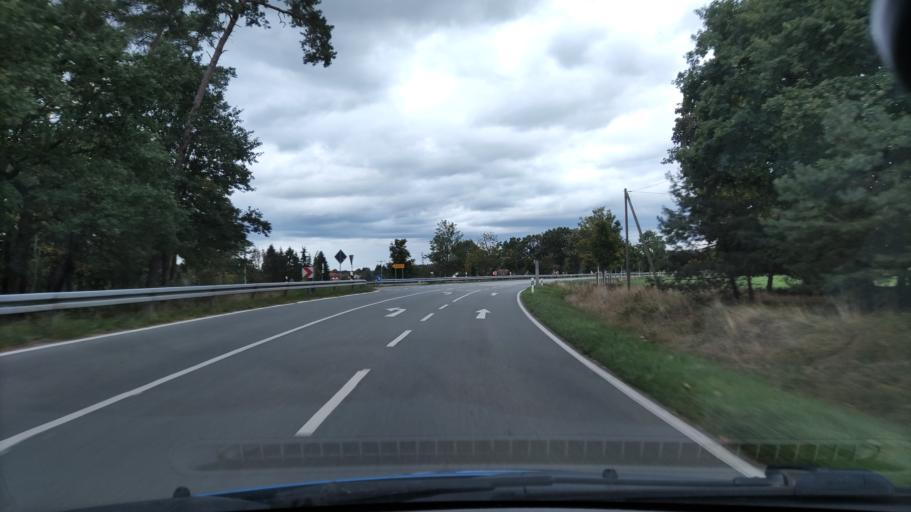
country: DE
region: Mecklenburg-Vorpommern
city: Lubtheen
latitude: 53.3556
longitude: 10.9575
